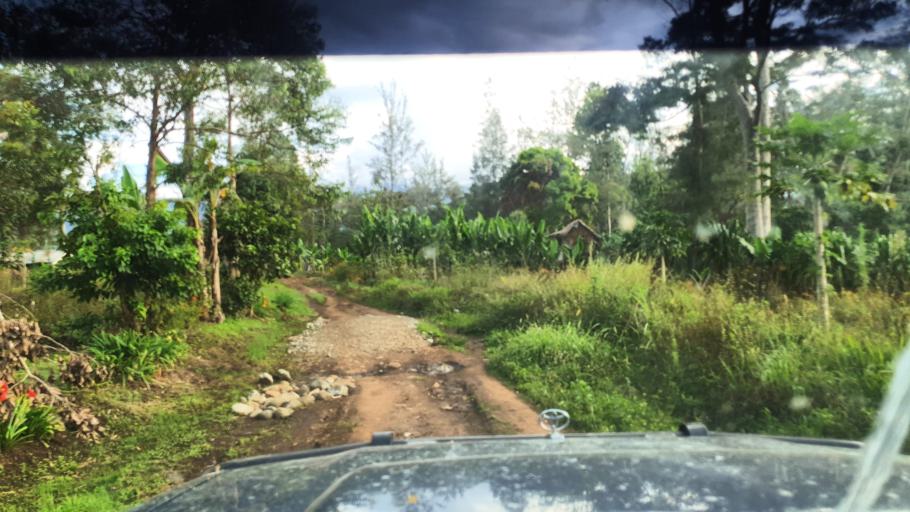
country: PG
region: Jiwaka
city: Minj
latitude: -5.9386
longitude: 144.8195
